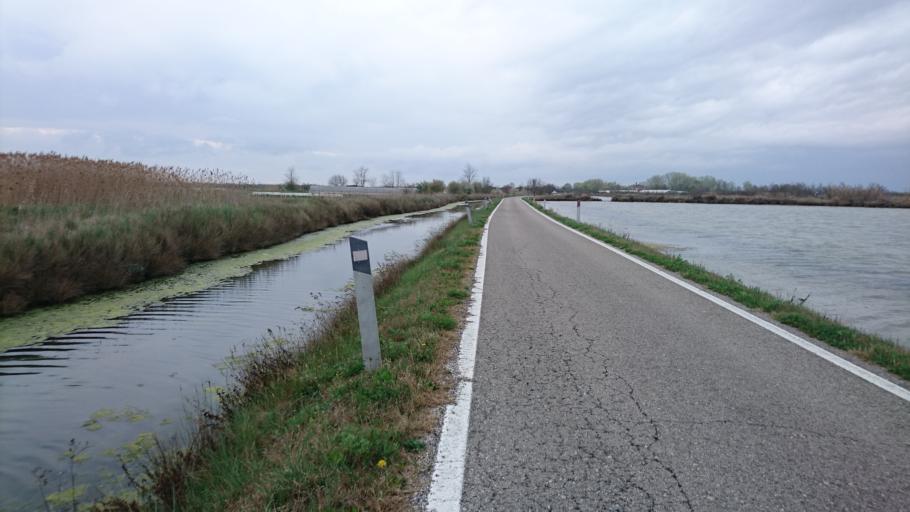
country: IT
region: Veneto
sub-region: Provincia di Venezia
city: Cavallino
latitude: 45.4912
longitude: 12.5027
